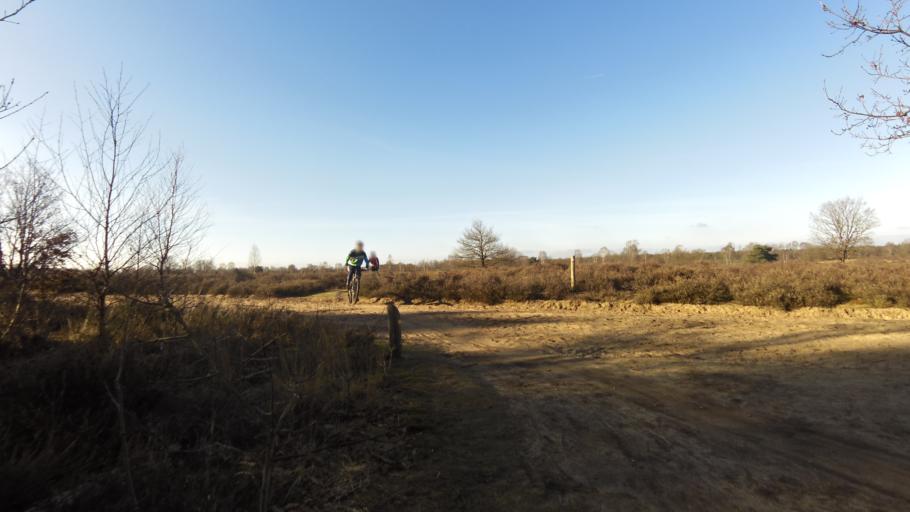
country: NL
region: Gelderland
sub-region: Gemeente Barneveld
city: Garderen
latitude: 52.2773
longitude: 5.6948
